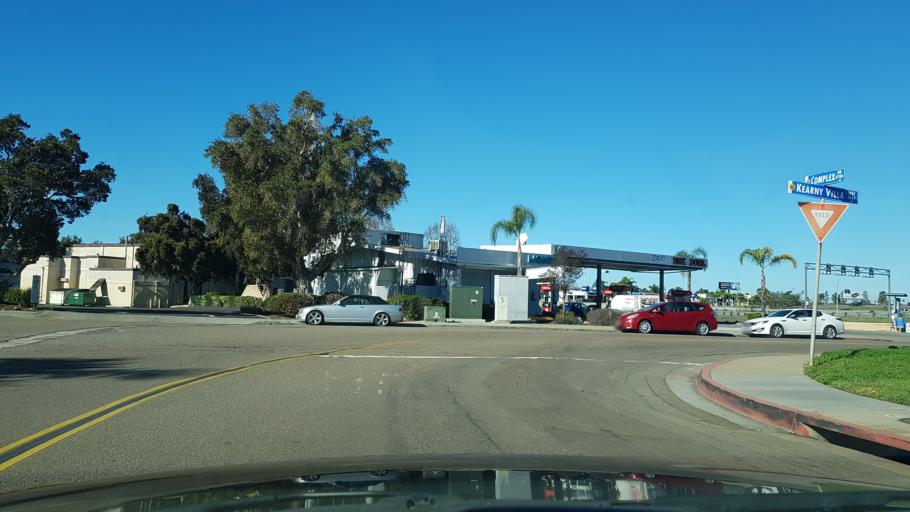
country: US
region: California
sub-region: San Diego County
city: San Diego
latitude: 32.8301
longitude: -117.1399
